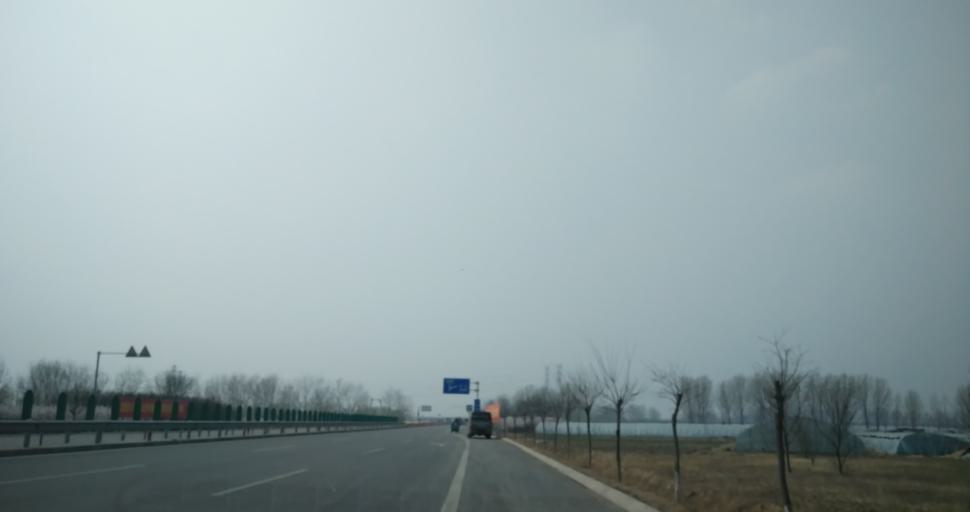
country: CN
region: Beijing
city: Qingyundian
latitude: 39.6878
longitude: 116.4604
